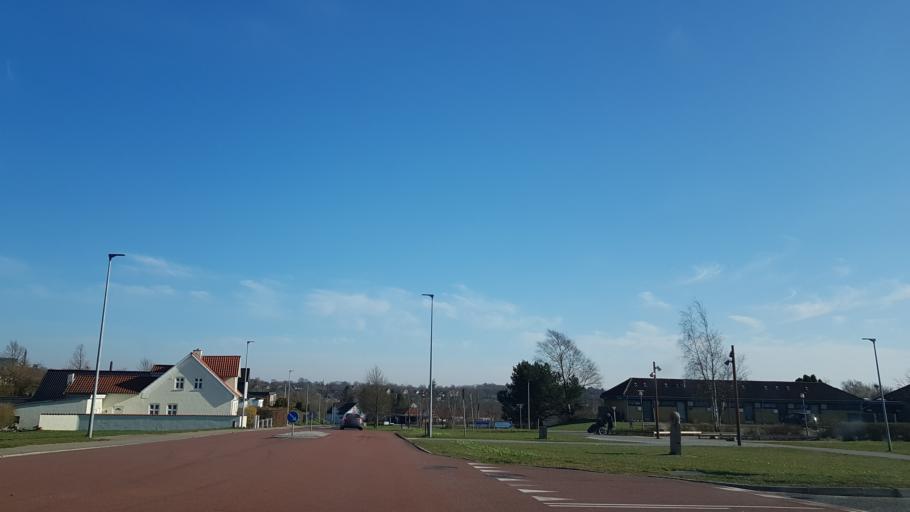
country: DK
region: South Denmark
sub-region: Kolding Kommune
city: Lunderskov
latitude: 55.4821
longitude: 9.2917
